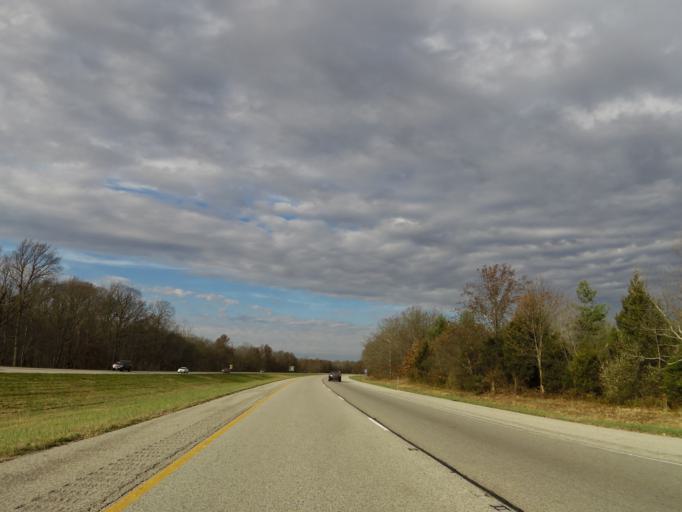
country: US
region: Illinois
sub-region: Washington County
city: Nashville
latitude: 38.3925
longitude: -89.3790
